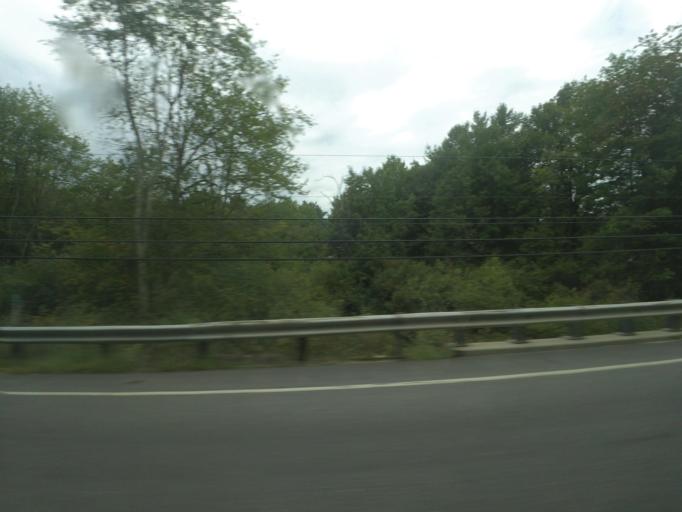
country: US
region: New Hampshire
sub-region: Strafford County
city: Rochester
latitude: 43.2858
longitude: -71.0035
